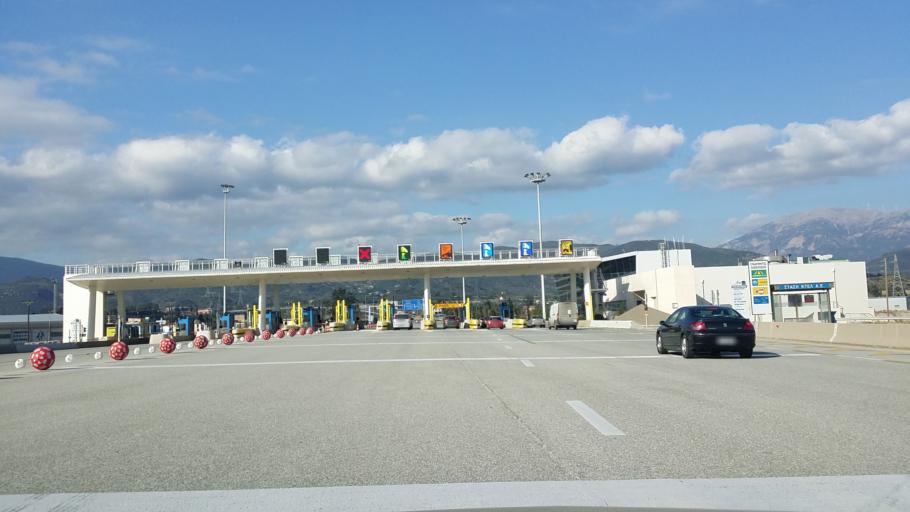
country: GR
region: West Greece
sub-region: Nomos Aitolias kai Akarnanias
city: Antirrio
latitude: 38.3328
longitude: 21.7665
